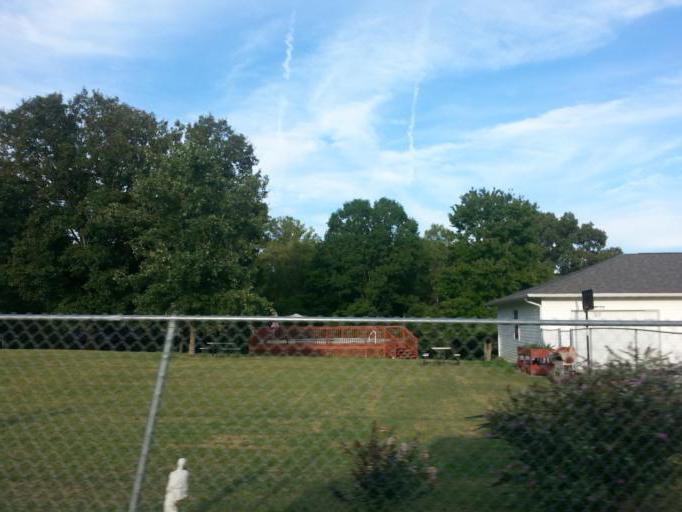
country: US
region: Tennessee
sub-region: Knox County
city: Knoxville
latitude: 35.9148
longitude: -83.8978
